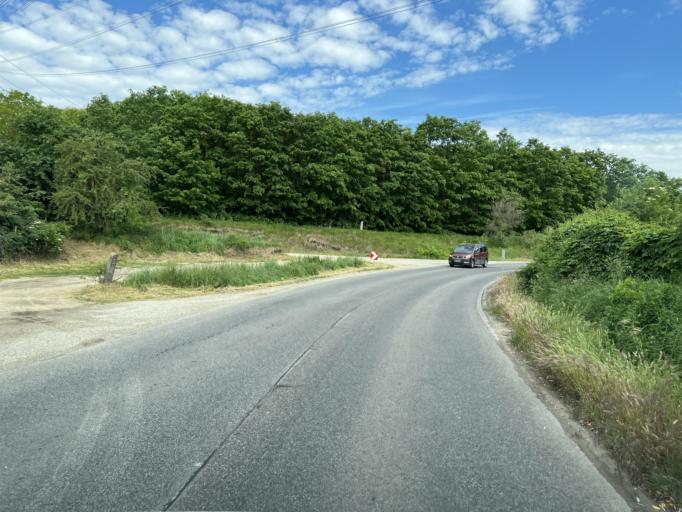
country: HU
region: Pest
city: Pecel
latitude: 47.5002
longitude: 19.3710
